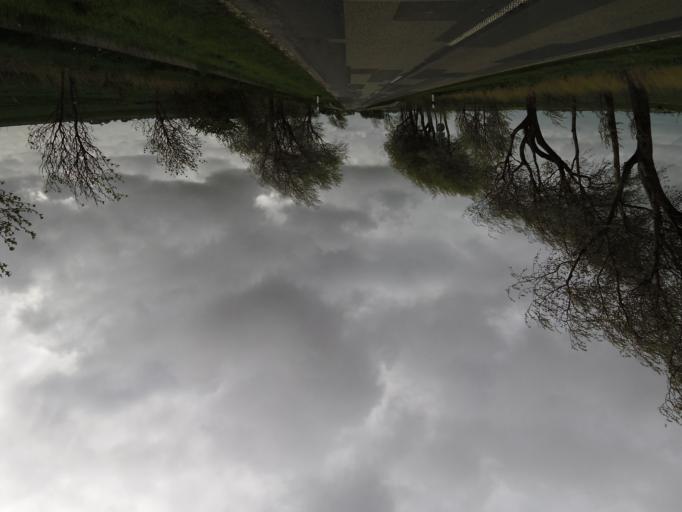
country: DE
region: Schleswig-Holstein
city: Galmsbull
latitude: 54.7644
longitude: 8.7520
